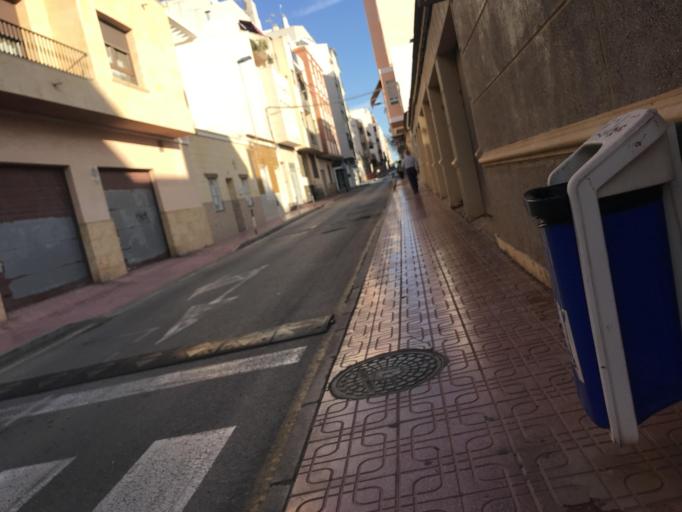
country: ES
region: Valencia
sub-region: Provincia de Alicante
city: Torrevieja
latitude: 37.9790
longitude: -0.6846
